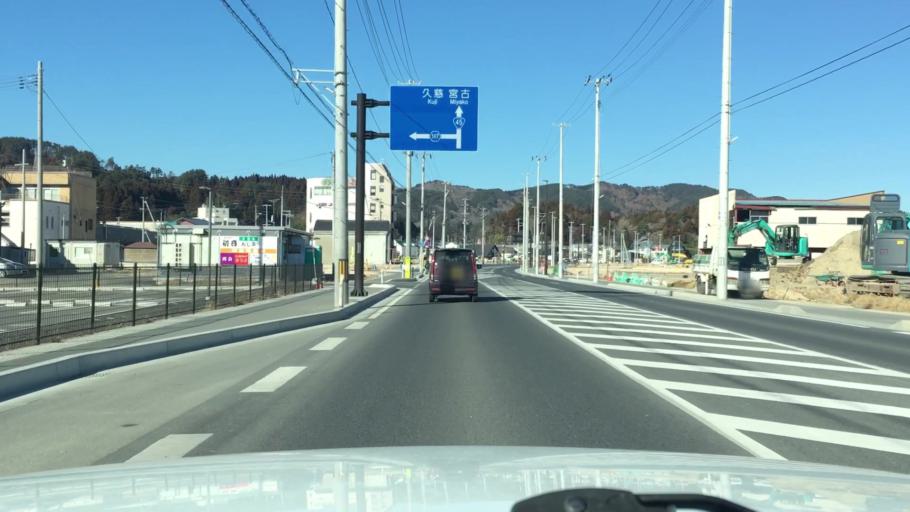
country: JP
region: Iwate
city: Yamada
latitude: 39.4638
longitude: 141.9535
